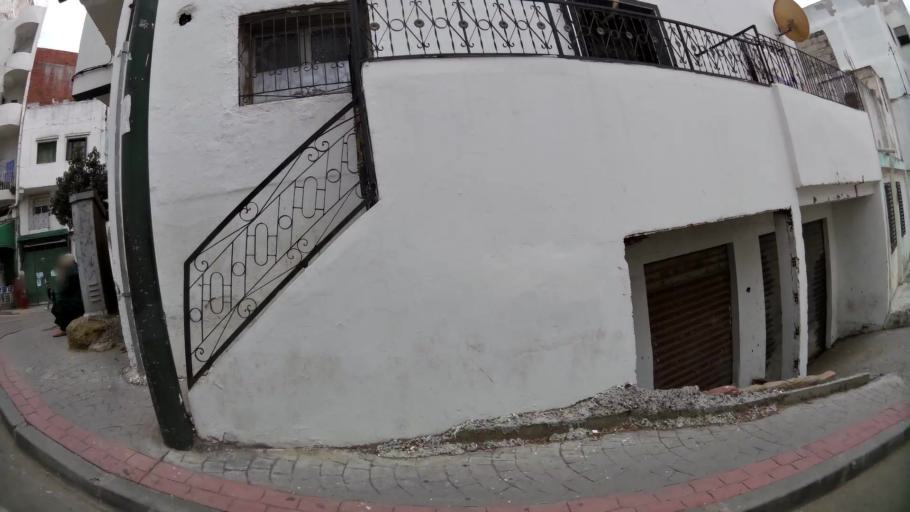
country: MA
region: Tanger-Tetouan
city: Tetouan
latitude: 35.5750
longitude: -5.3910
